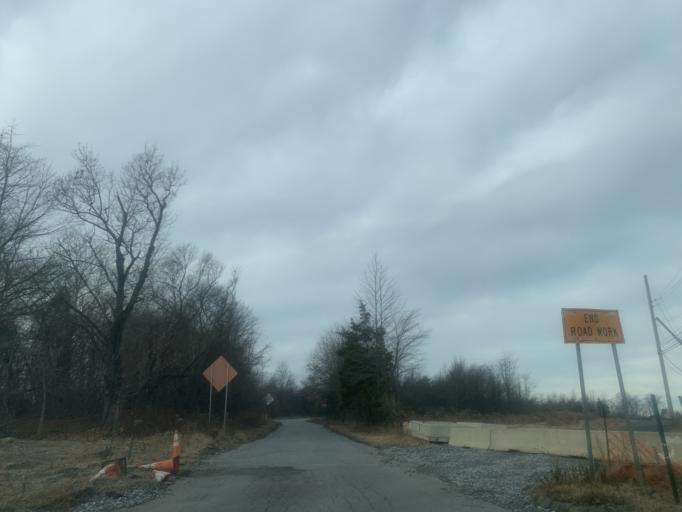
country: US
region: Maryland
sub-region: Prince George's County
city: Forestville
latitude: 38.8309
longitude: -76.8546
